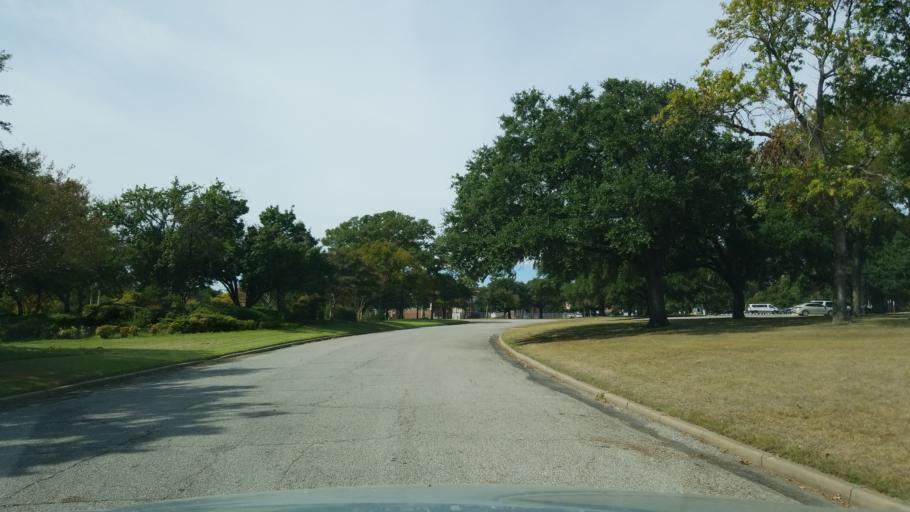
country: US
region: Texas
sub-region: Dallas County
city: Highland Park
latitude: 32.7961
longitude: -96.7406
